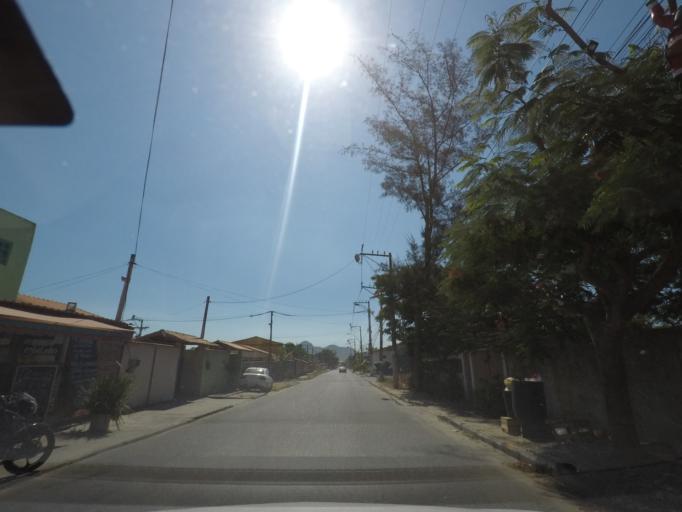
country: BR
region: Rio de Janeiro
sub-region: Marica
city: Marica
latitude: -22.9671
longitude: -42.9572
